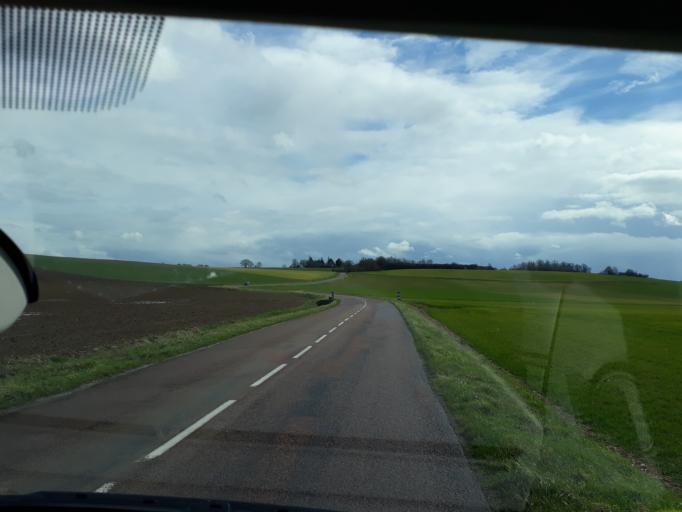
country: FR
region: Bourgogne
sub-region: Departement de la Cote-d'Or
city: Genlis
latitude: 47.2159
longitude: 5.1942
